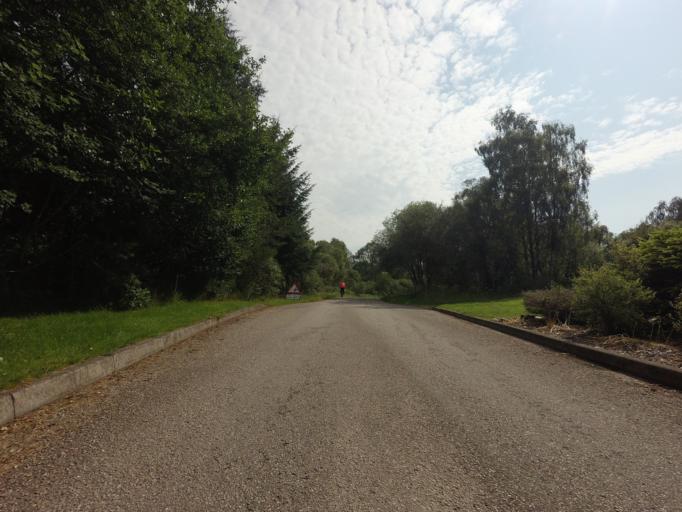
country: GB
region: Scotland
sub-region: Highland
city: Evanton
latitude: 57.9595
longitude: -4.4074
